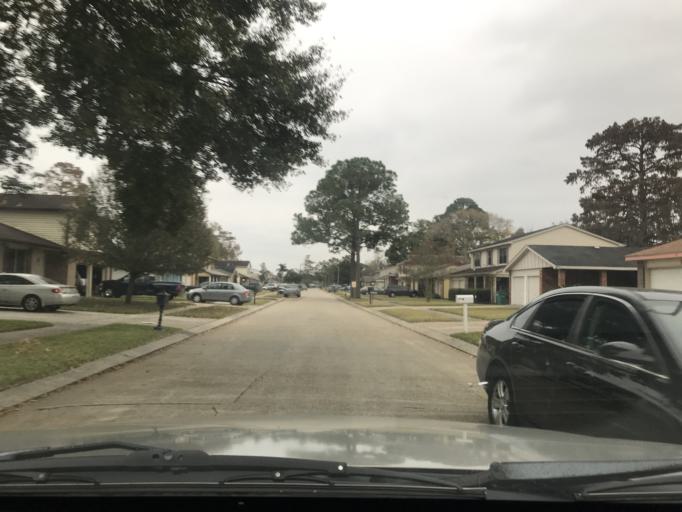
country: US
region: Louisiana
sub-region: Jefferson Parish
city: Woodmere
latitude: 29.8661
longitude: -90.0799
